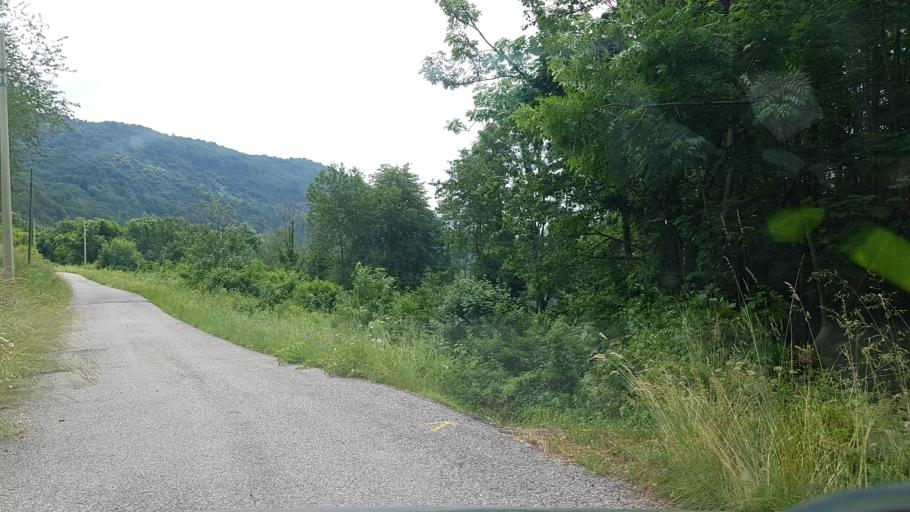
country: IT
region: Friuli Venezia Giulia
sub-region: Provincia di Udine
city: Torreano
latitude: 46.1767
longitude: 13.4300
